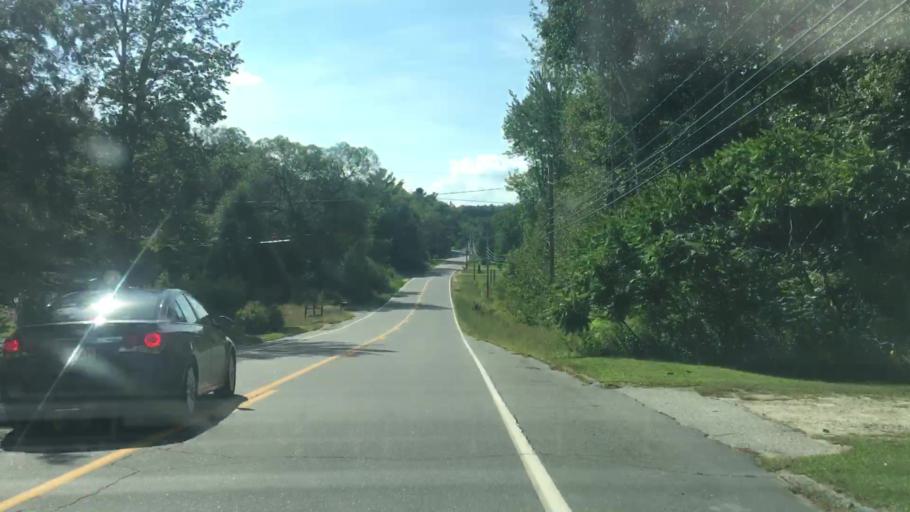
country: US
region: Maine
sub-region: Sagadahoc County
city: North Bath
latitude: 43.9332
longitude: -69.8705
